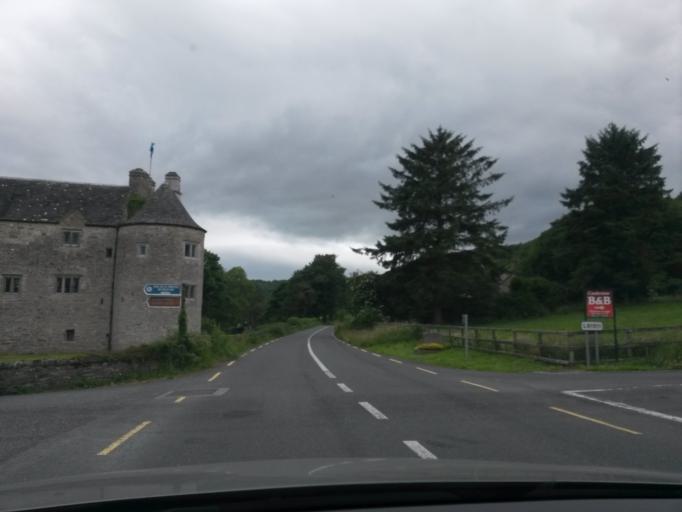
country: IE
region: Connaught
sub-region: Sligo
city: Sligo
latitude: 54.2648
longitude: -8.3337
